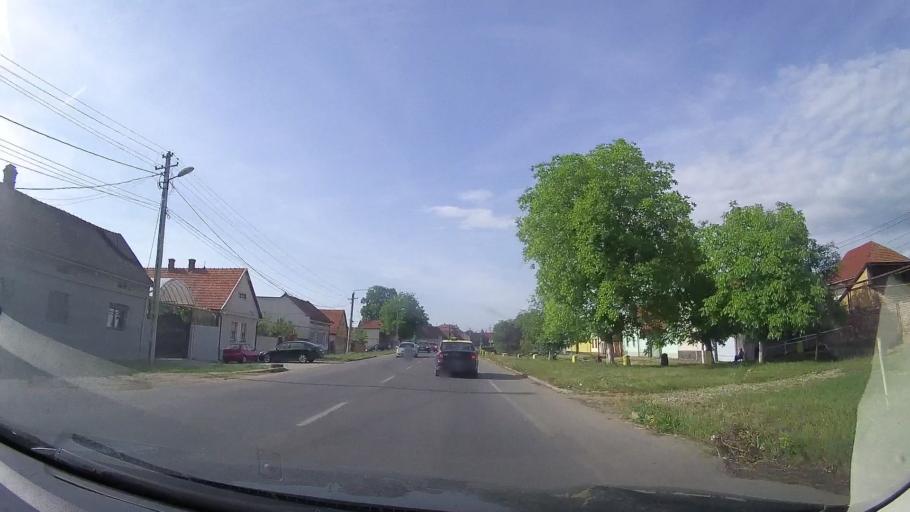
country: RO
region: Caras-Severin
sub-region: Municipiul Caransebes
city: Caransebes
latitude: 45.4013
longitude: 22.2243
